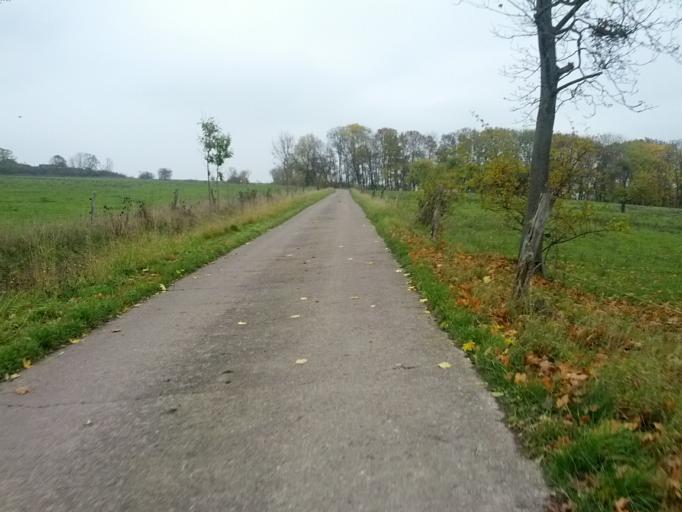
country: DE
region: Thuringia
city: Seebach
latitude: 50.9819
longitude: 10.4372
